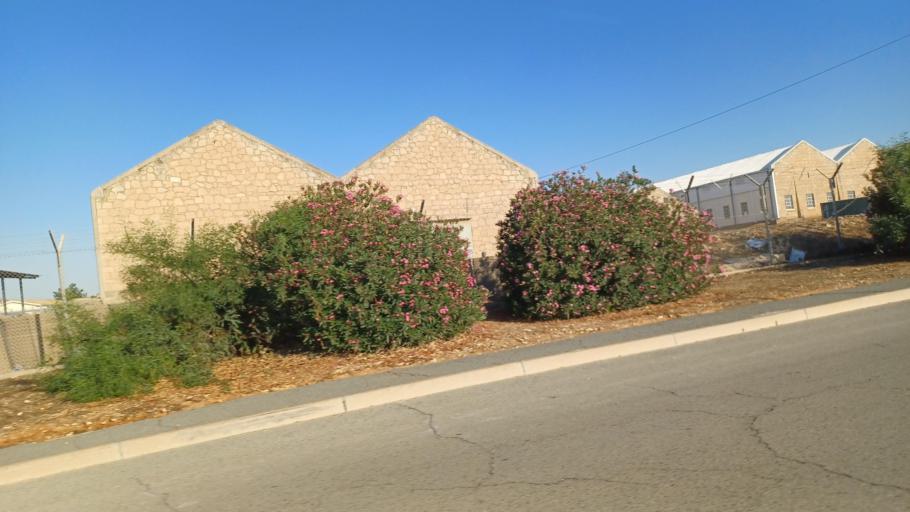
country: CY
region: Larnaka
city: Xylotymbou
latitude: 34.9982
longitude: 33.7422
